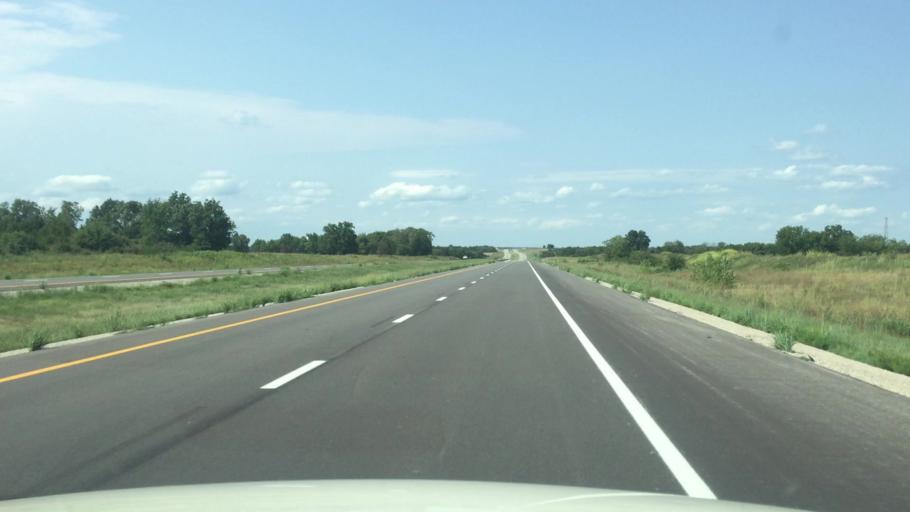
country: US
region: Kansas
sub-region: Linn County
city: La Cygne
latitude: 38.3763
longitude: -94.6874
